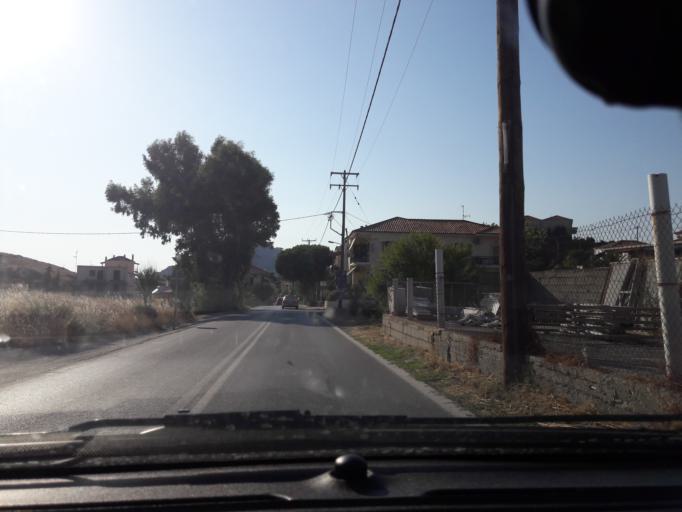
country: GR
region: North Aegean
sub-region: Nomos Lesvou
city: Myrina
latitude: 39.8715
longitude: 25.0676
